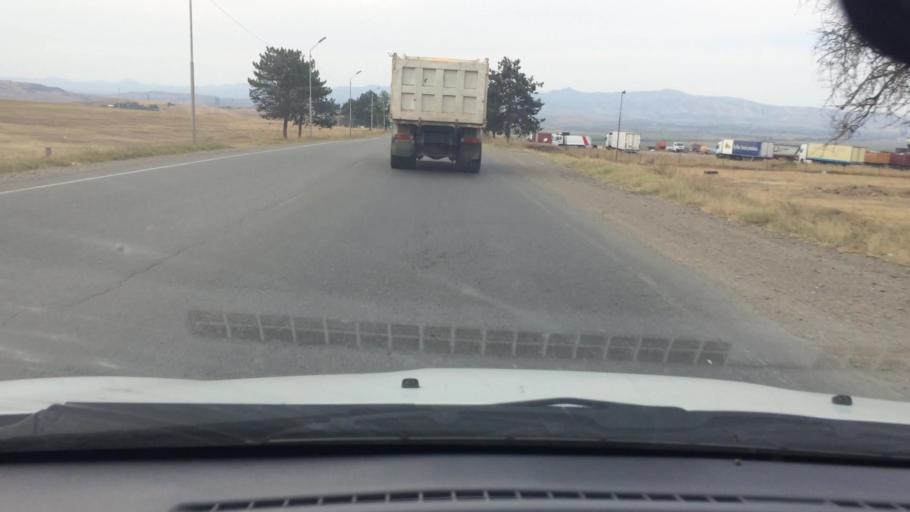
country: GE
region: Kvemo Kartli
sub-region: Marneuli
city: Marneuli
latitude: 41.5116
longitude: 44.7909
